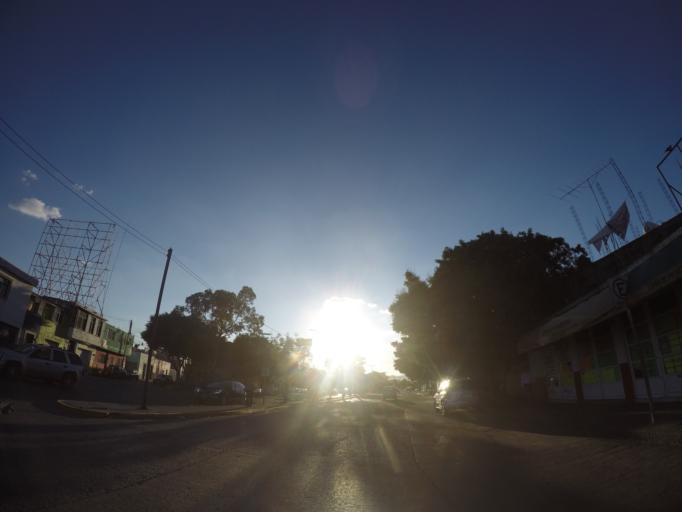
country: MX
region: San Luis Potosi
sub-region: San Luis Potosi
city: San Luis Potosi
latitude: 22.1333
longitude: -100.9741
